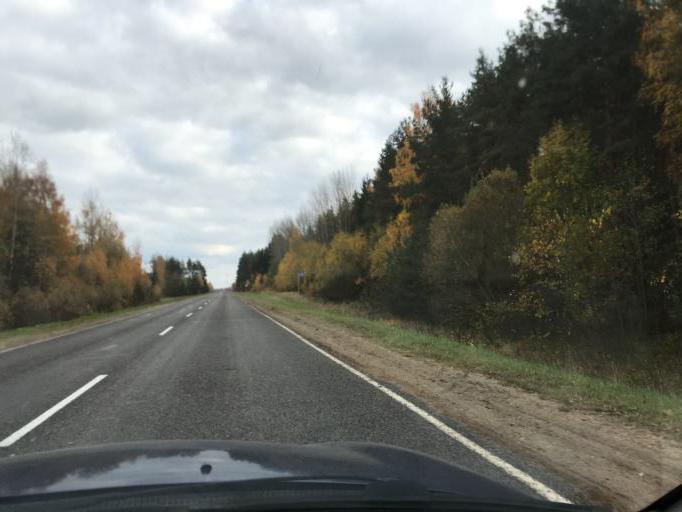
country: BY
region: Grodnenskaya
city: Lida
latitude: 53.7431
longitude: 25.3372
